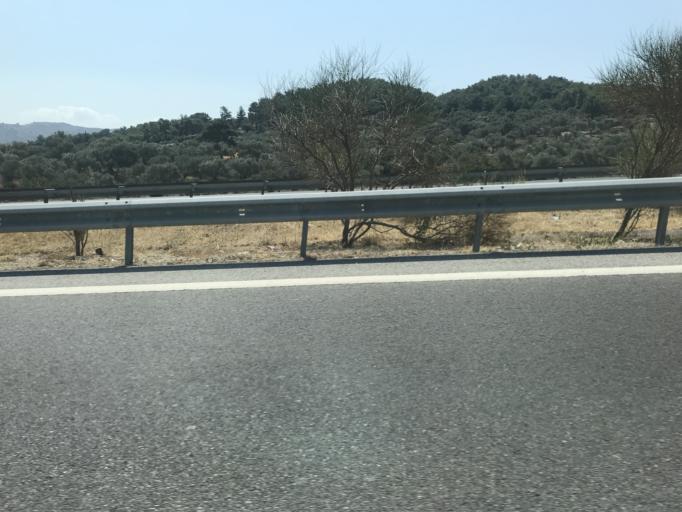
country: TR
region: Izmir
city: Urla
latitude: 38.3495
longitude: 26.8467
